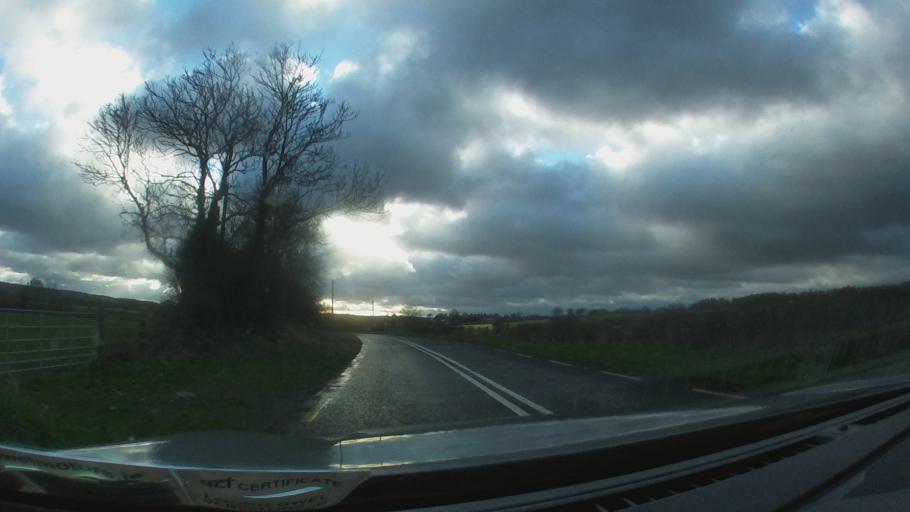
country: IE
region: Leinster
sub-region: Kilkenny
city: Thomastown
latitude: 52.5643
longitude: -7.1193
